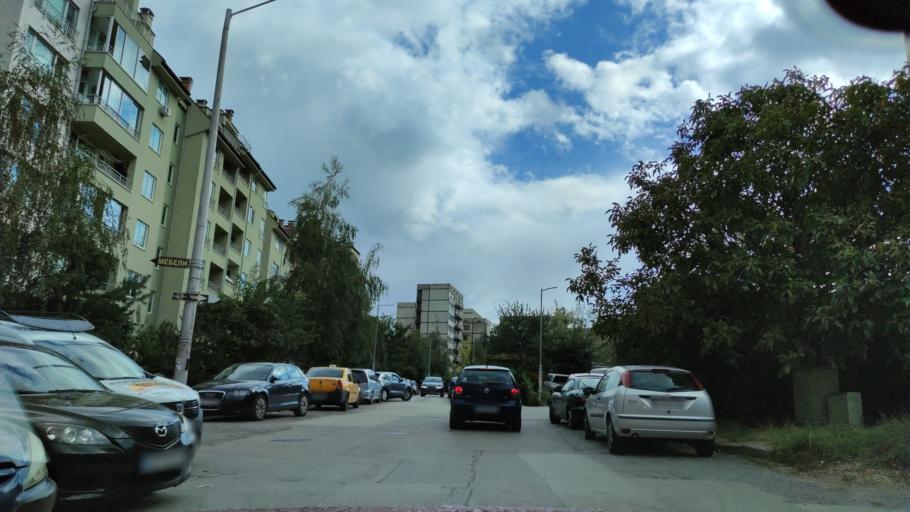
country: BG
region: Sofia-Capital
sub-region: Stolichna Obshtina
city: Sofia
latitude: 42.6576
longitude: 23.3431
